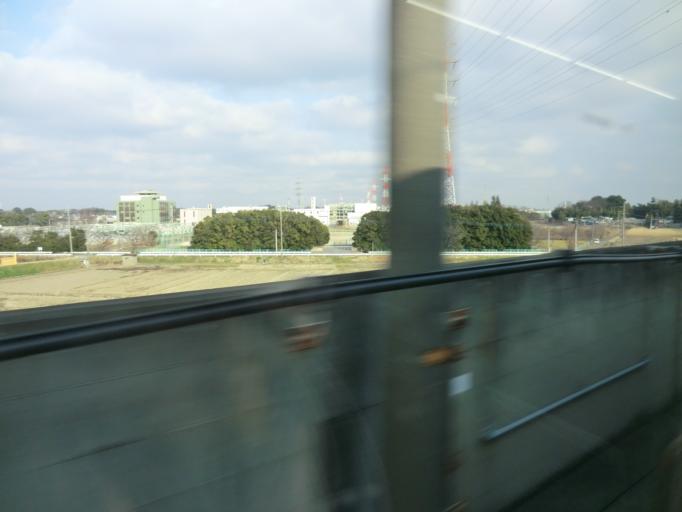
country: JP
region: Saitama
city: Okegawa
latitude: 36.0247
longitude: 139.5867
